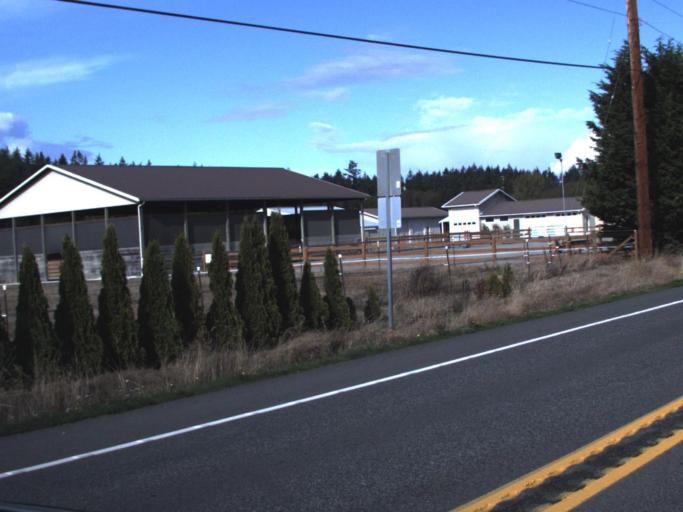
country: US
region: Washington
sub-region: Island County
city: Coupeville
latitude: 48.2510
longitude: -122.7118
